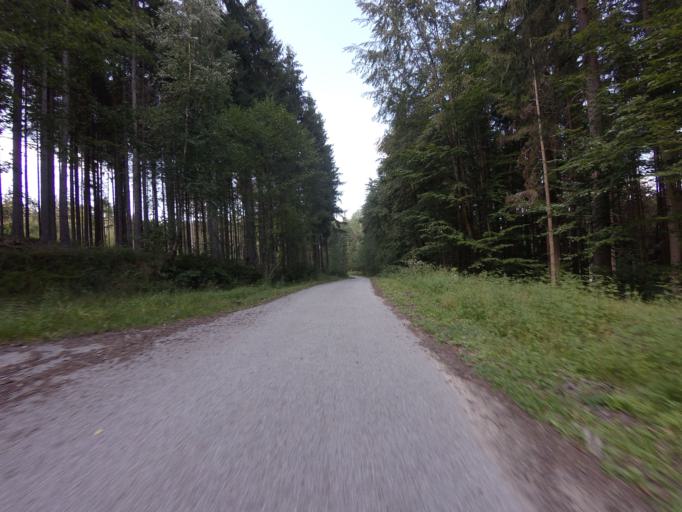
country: CZ
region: Jihocesky
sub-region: Okres Ceske Budejovice
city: Hluboka nad Vltavou
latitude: 49.1076
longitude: 14.4599
